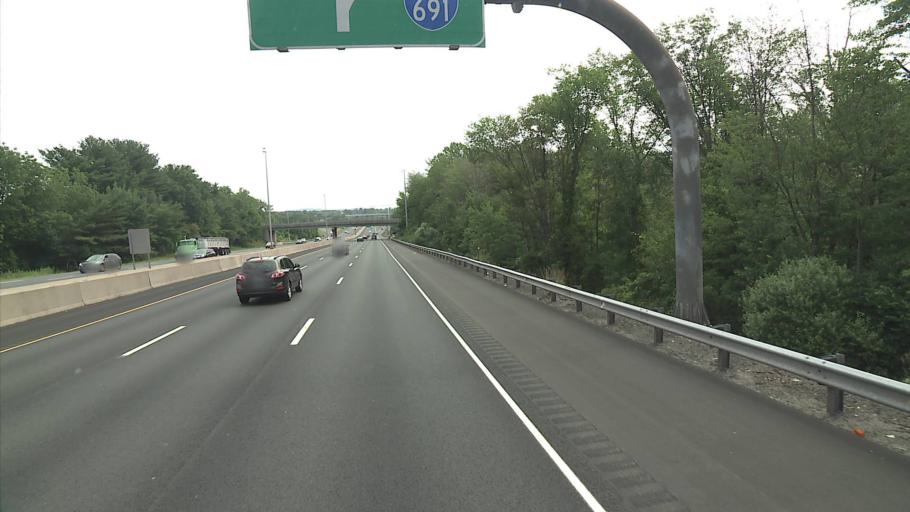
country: US
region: Connecticut
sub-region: New Haven County
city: Cheshire Village
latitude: 41.5556
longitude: -72.9274
